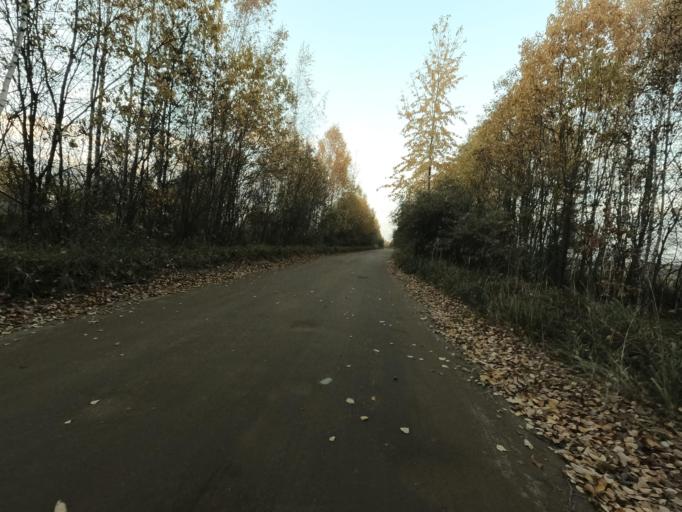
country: RU
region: Leningrad
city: Mga
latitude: 59.7937
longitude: 31.2008
